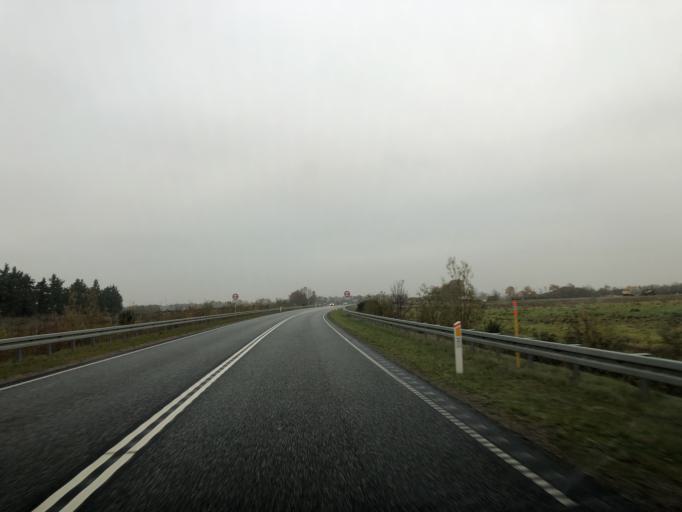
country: DK
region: Central Jutland
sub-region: Herning Kommune
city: Sunds
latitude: 56.2096
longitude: 8.9915
